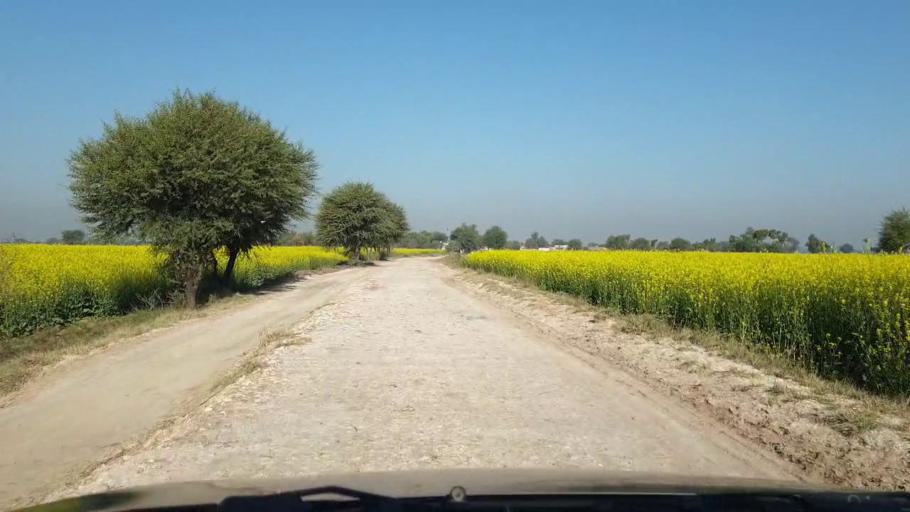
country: PK
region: Sindh
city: Jhol
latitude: 25.9370
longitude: 68.8420
